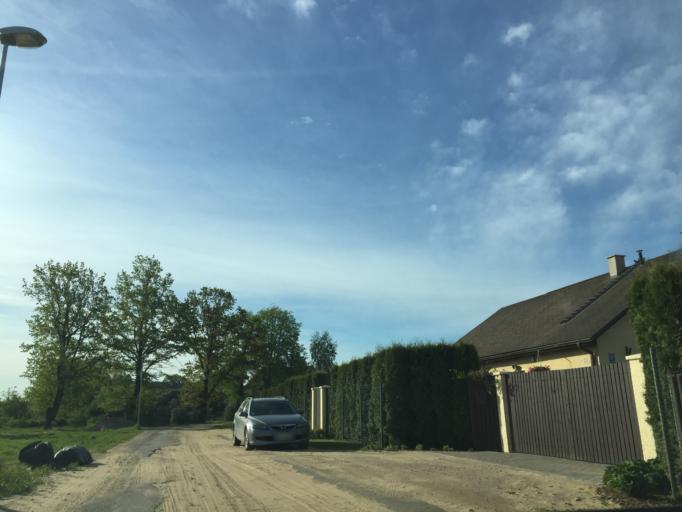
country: LV
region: Lecava
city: Iecava
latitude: 56.6028
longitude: 24.2062
